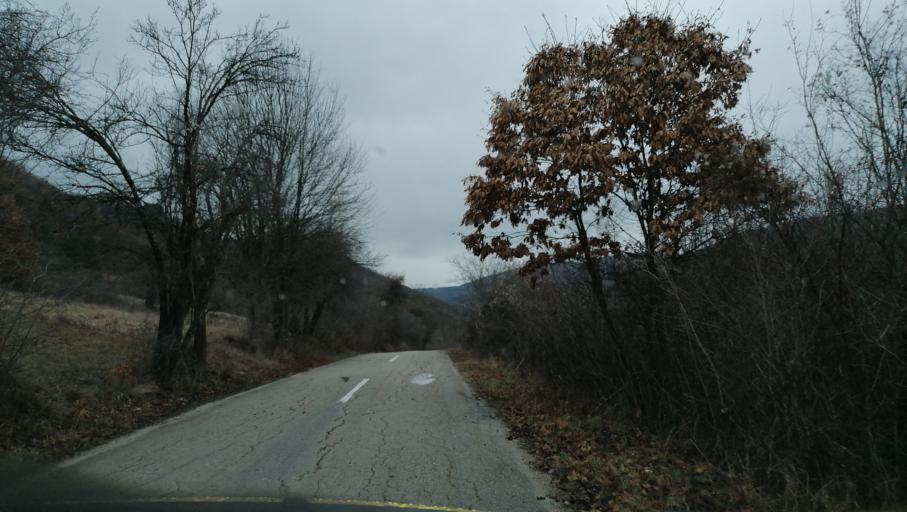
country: RS
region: Central Serbia
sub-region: Pirotski Okrug
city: Dimitrovgrad
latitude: 42.9584
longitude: 22.7826
